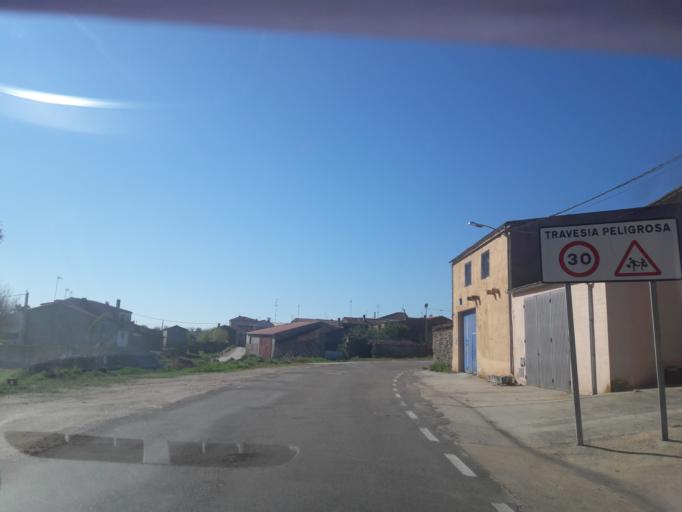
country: ES
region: Castille and Leon
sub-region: Provincia de Salamanca
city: Valsalabroso
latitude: 41.1552
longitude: -6.4880
